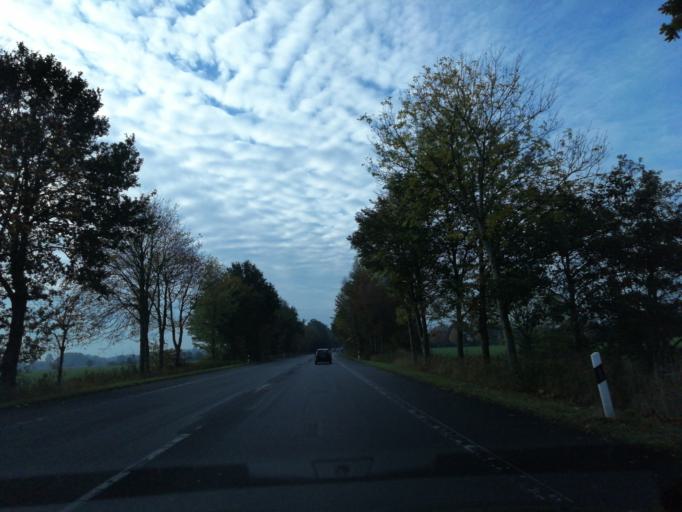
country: DE
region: Lower Saxony
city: Fedderwarden
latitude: 53.5644
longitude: 8.0539
